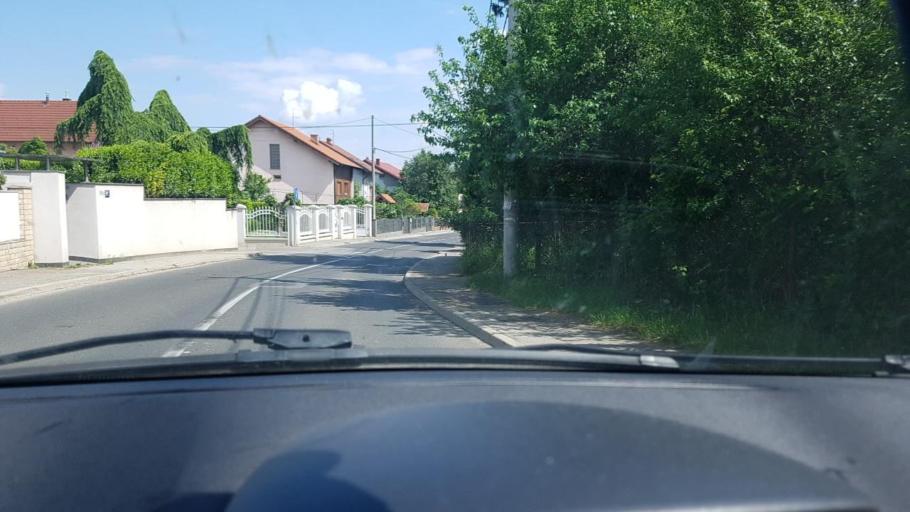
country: HR
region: Grad Zagreb
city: Zagreb
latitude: 45.8407
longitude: 16.0169
